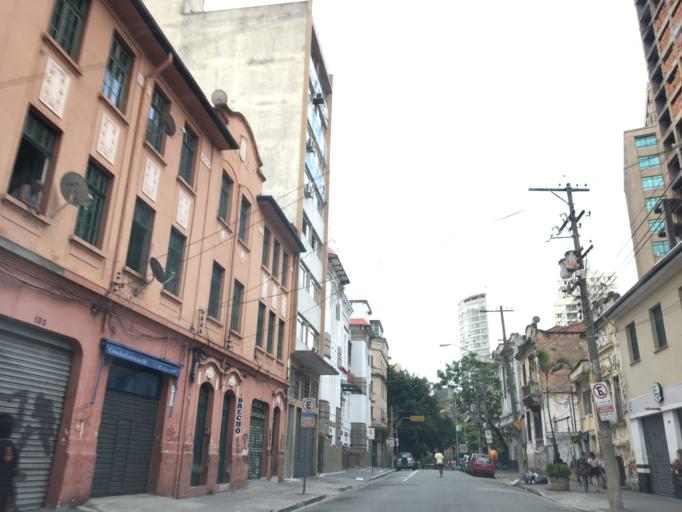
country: BR
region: Sao Paulo
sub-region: Sao Paulo
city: Sao Paulo
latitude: -23.5517
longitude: -46.6303
